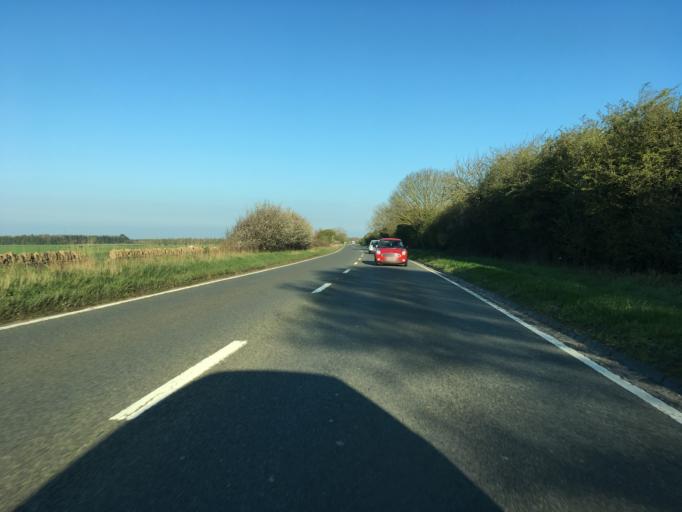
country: GB
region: England
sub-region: Oxfordshire
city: Burford
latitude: 51.8061
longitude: -1.6521
